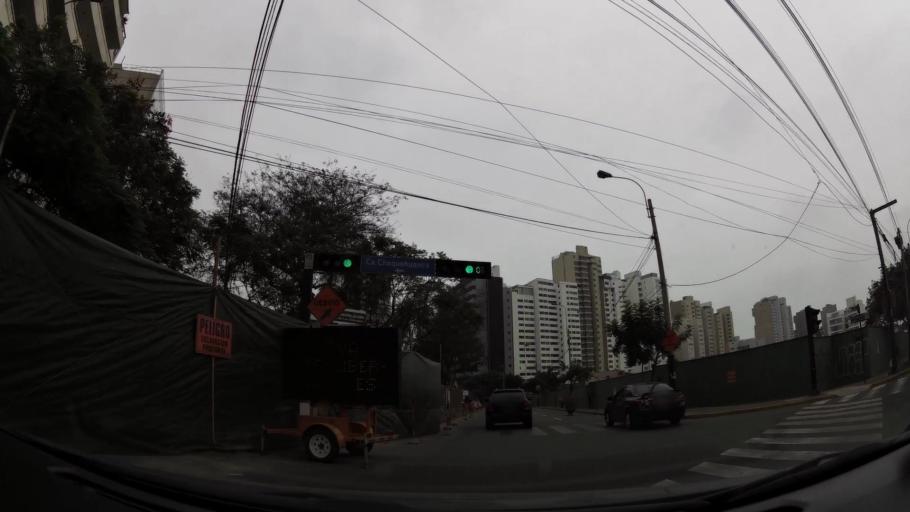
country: PE
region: Lima
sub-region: Lima
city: San Isidro
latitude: -12.0990
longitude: -77.0372
